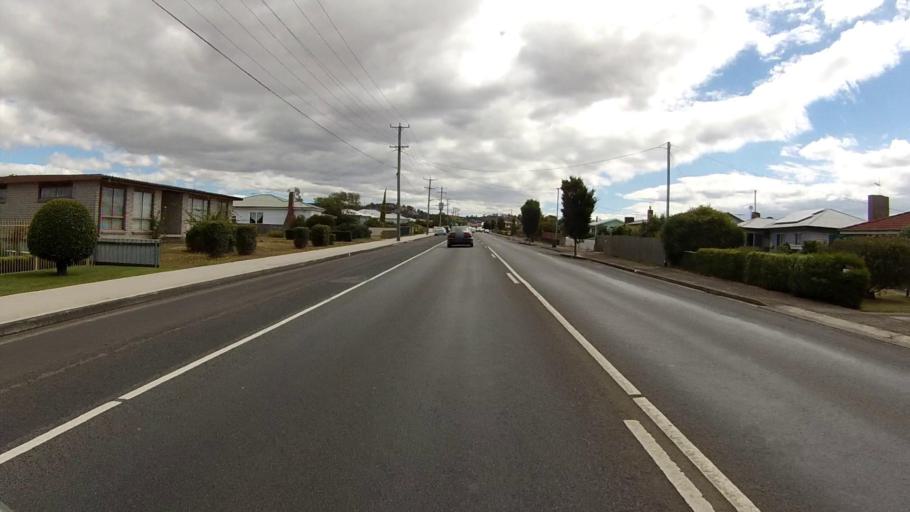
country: AU
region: Tasmania
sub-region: Sorell
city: Sorell
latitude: -42.7898
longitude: 147.5615
